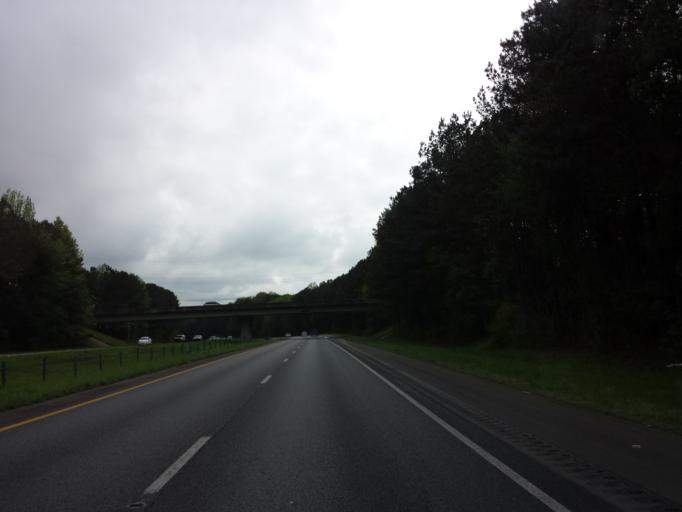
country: US
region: Georgia
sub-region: Cherokee County
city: Holly Springs
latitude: 34.1983
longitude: -84.5005
